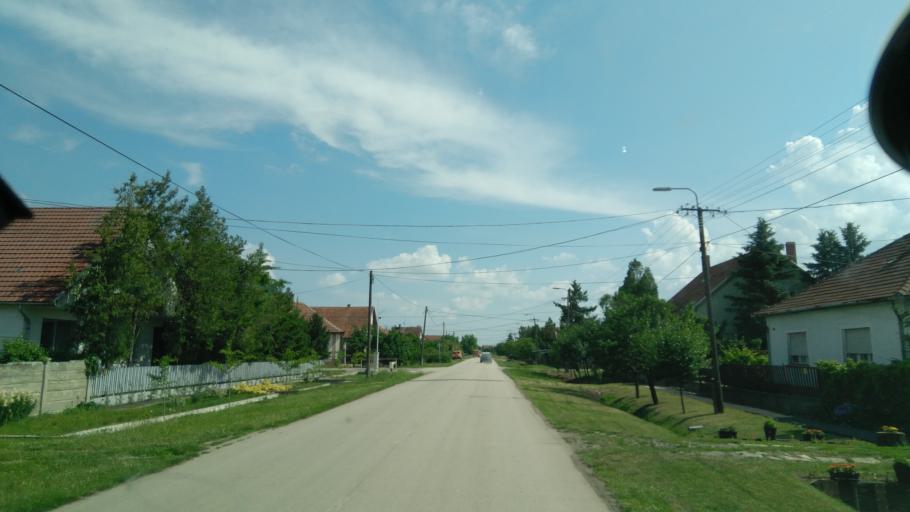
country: HU
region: Bekes
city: Doboz
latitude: 46.7385
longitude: 21.2364
